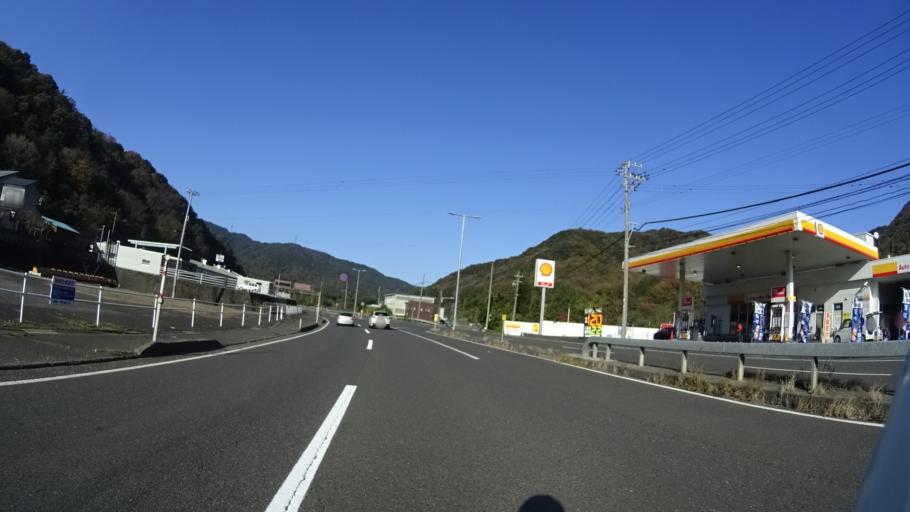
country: JP
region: Fukui
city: Tsuruga
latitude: 35.6046
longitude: 136.0966
